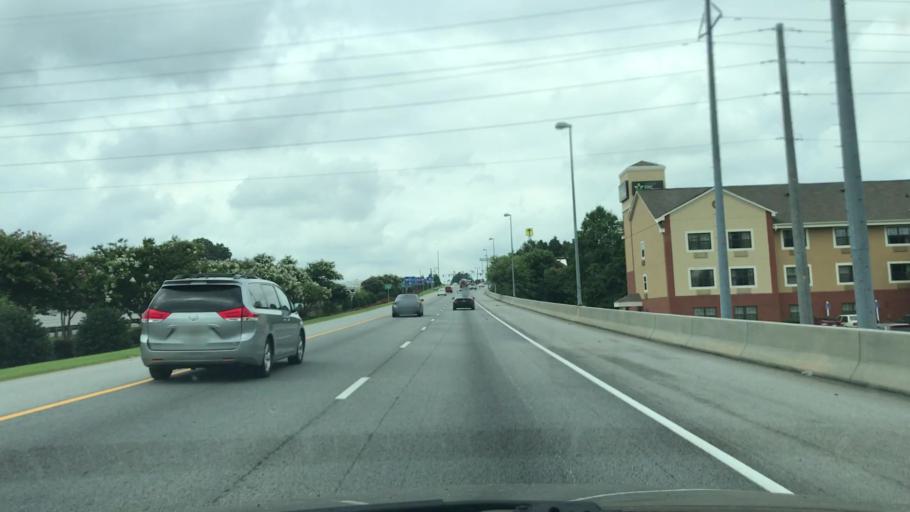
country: US
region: Georgia
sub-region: Gwinnett County
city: Duluth
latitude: 33.9550
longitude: -84.1255
